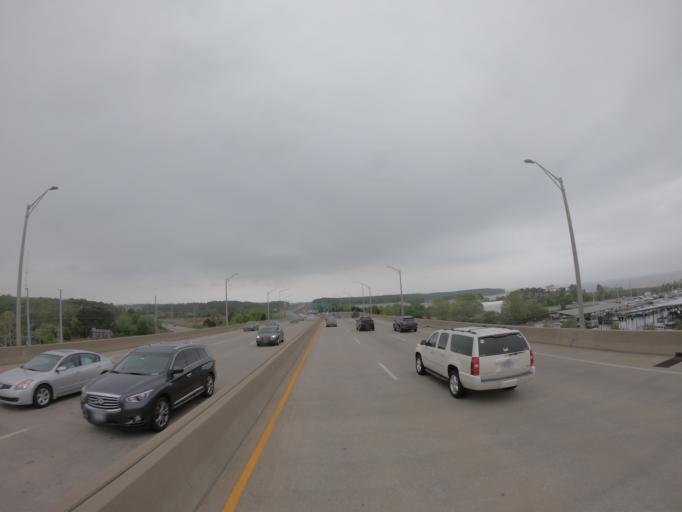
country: US
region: Maryland
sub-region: Queen Anne's County
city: Chester
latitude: 38.9718
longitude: -76.2515
